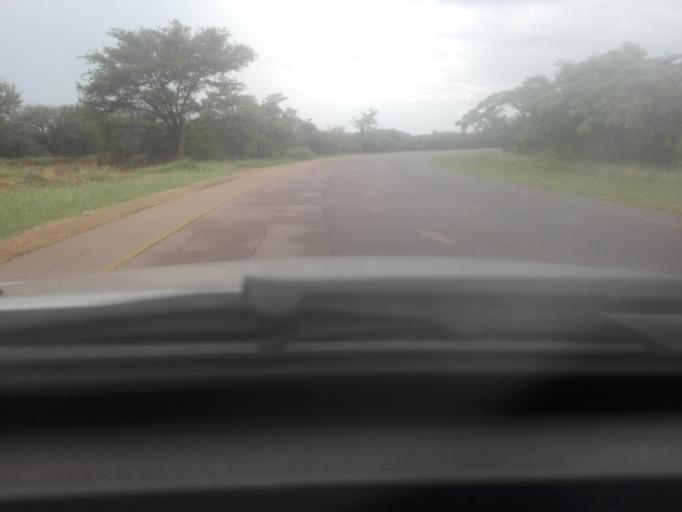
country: BW
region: Kweneng
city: Mmopone
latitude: -24.5578
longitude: 25.9284
